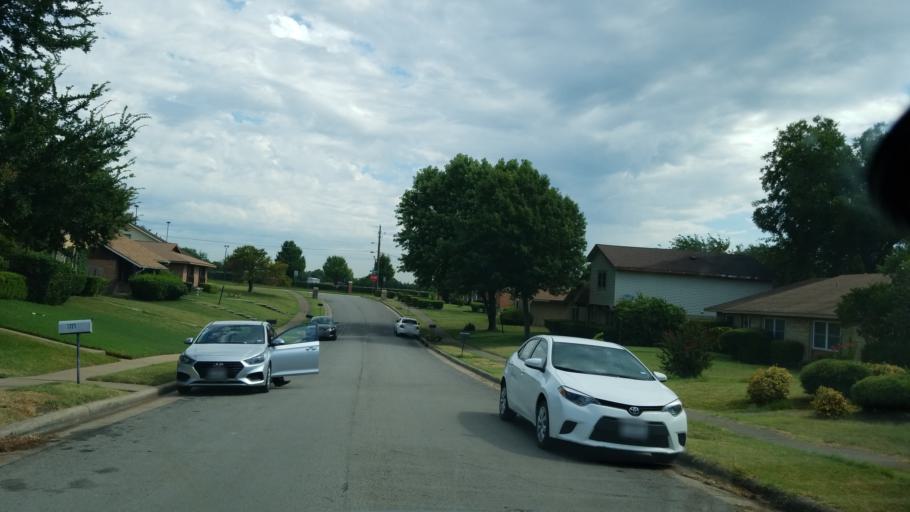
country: US
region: Texas
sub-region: Dallas County
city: Duncanville
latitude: 32.6540
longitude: -96.8535
